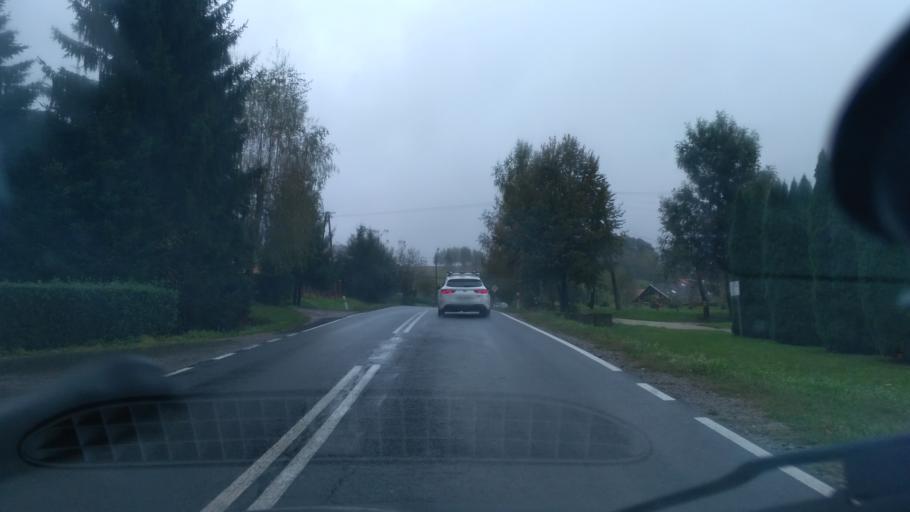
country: PL
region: Subcarpathian Voivodeship
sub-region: Powiat ropczycko-sedziszowski
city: Wielopole Skrzynskie
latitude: 49.9747
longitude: 21.5724
